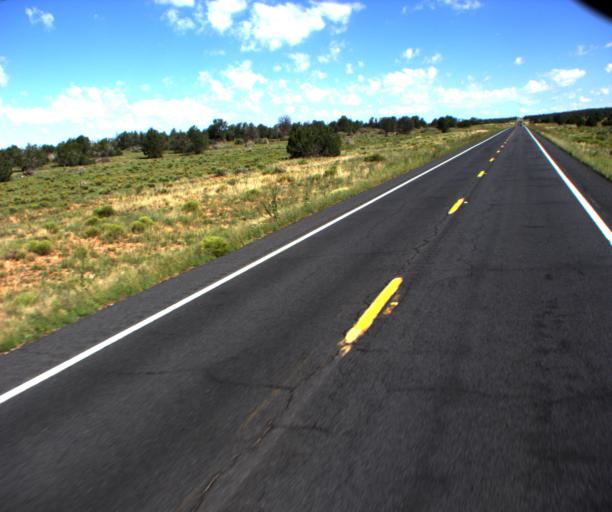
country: US
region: Arizona
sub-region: Coconino County
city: Grand Canyon Village
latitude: 35.7922
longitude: -112.1301
